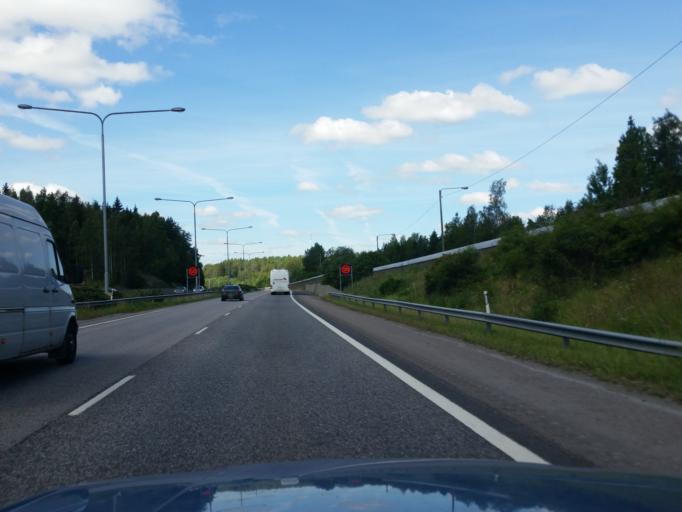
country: FI
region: Uusimaa
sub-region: Helsinki
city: Espoo
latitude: 60.2221
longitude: 24.6308
